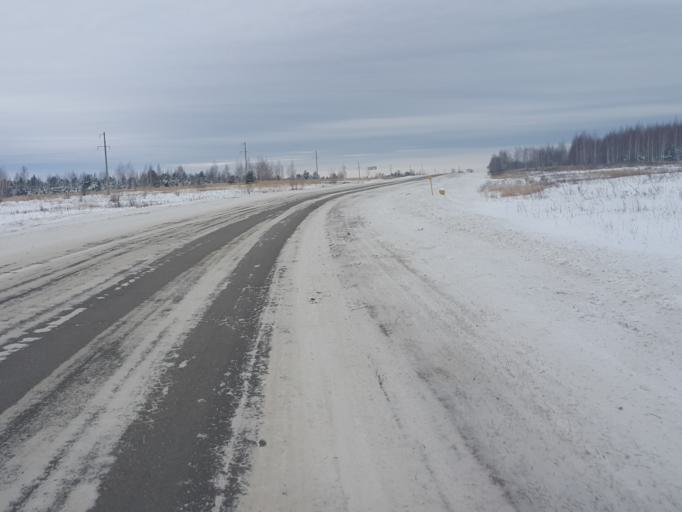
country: RU
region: Tambov
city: Platonovka
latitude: 52.8725
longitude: 41.8710
